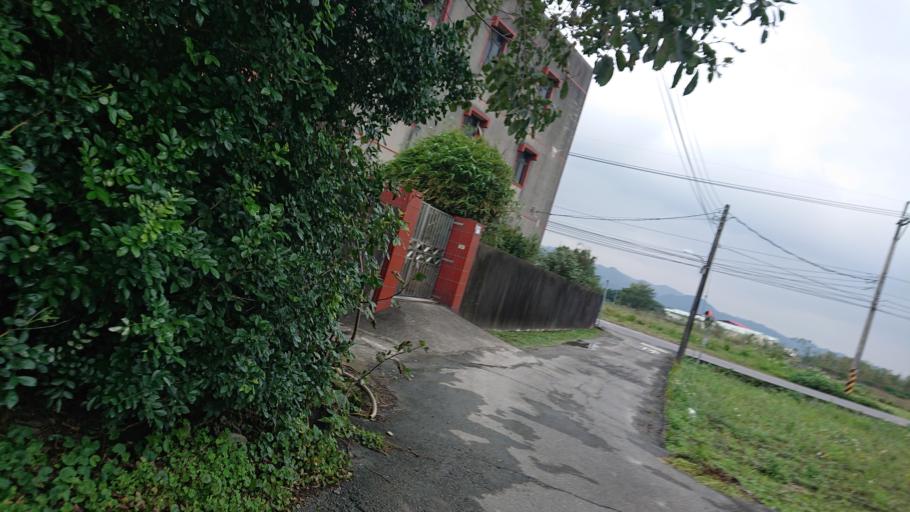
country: TW
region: Taiwan
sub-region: Taoyuan
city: Taoyuan
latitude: 24.9424
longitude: 121.3873
